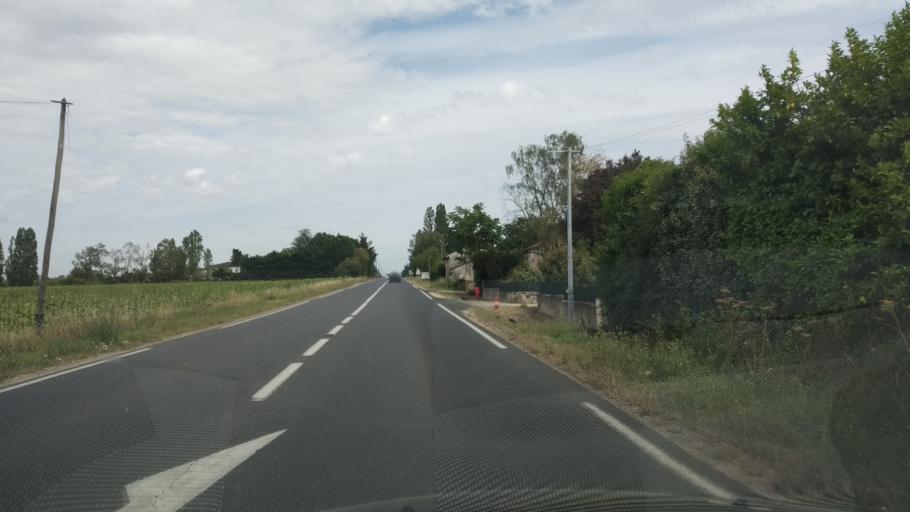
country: FR
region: Poitou-Charentes
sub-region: Departement de la Vienne
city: Mignaloux-Beauvoir
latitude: 46.5611
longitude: 0.4358
